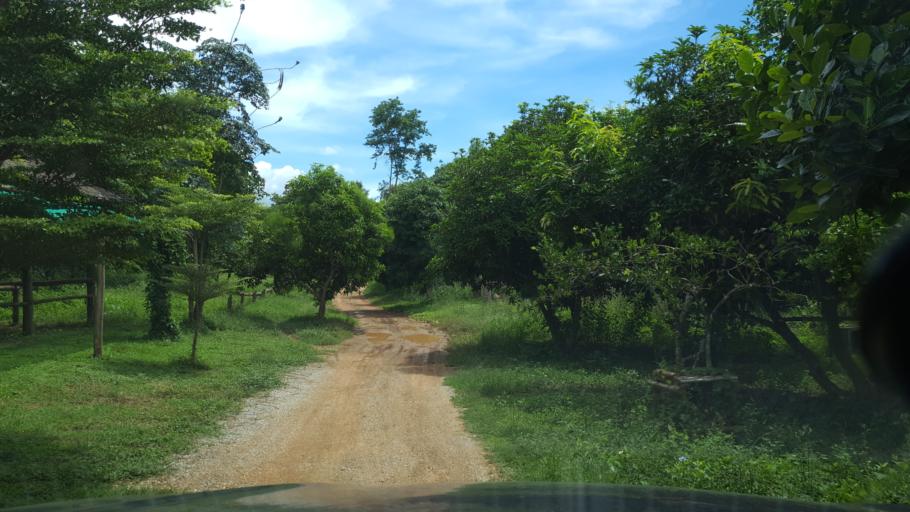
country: TH
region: Sukhothai
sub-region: Amphoe Si Satchanalai
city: Si Satchanalai
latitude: 17.6646
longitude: 99.6869
